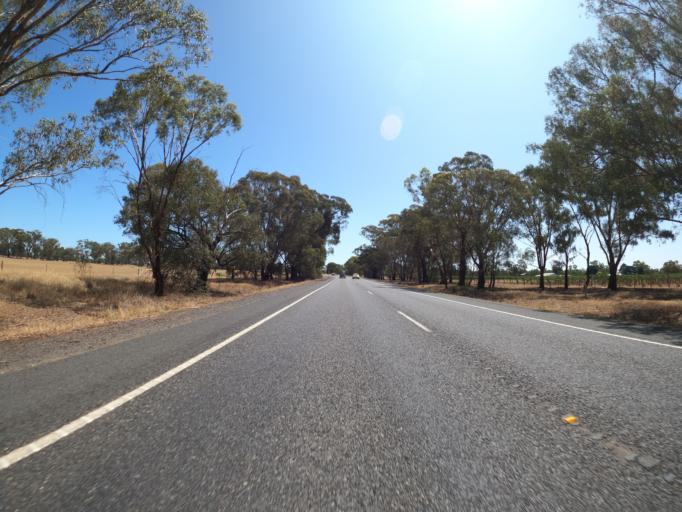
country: AU
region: New South Wales
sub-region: Corowa Shire
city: Corowa
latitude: -36.0628
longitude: 146.3995
